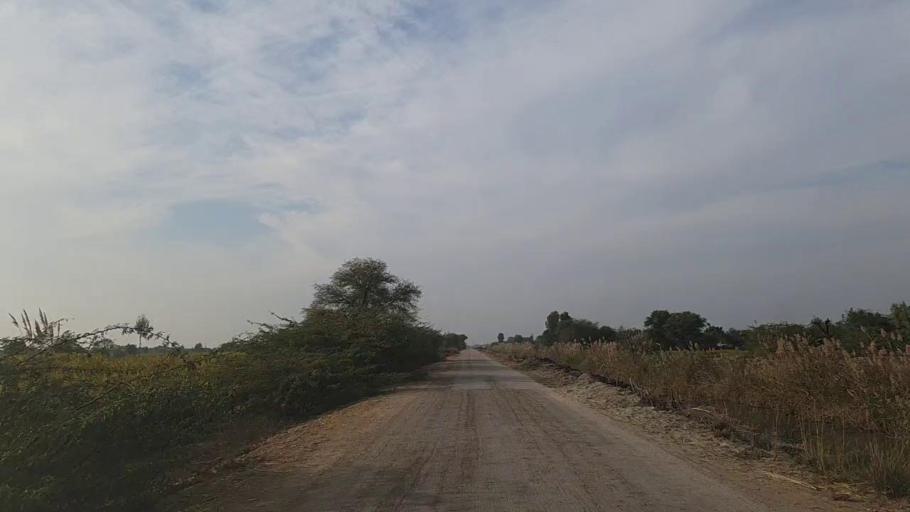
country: PK
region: Sindh
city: Daur
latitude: 26.4943
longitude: 68.4537
